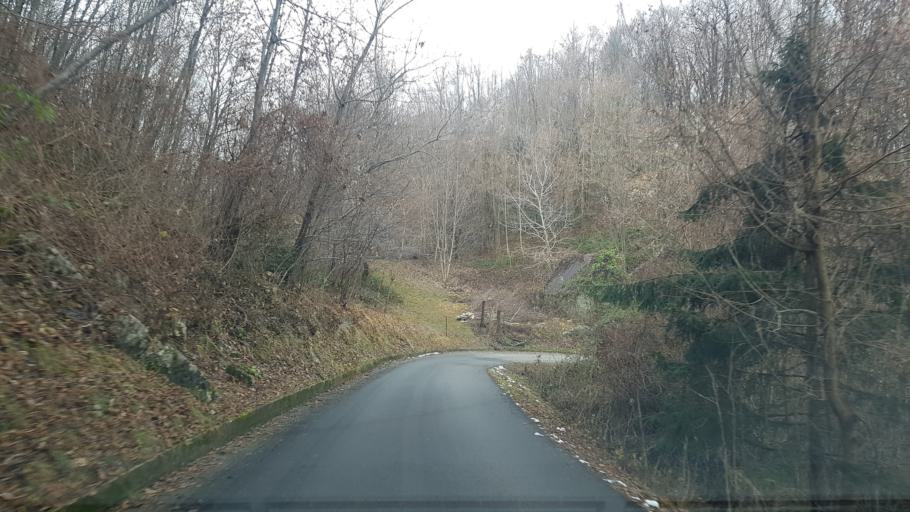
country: IT
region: Friuli Venezia Giulia
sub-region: Provincia di Udine
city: Savogna
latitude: 46.1730
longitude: 13.5515
